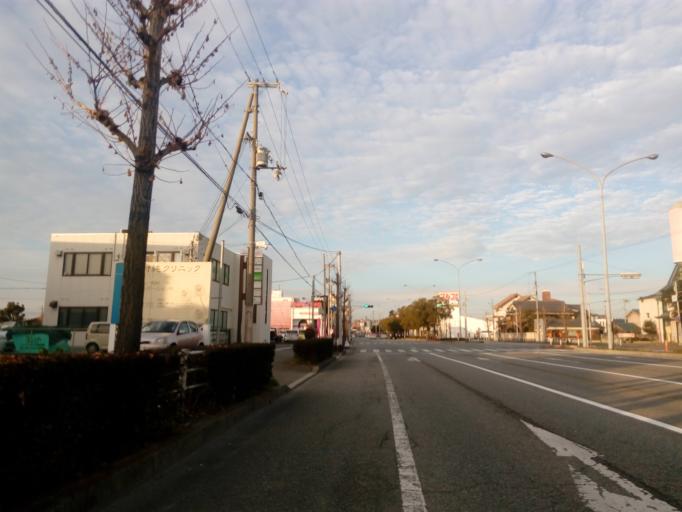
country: JP
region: Hyogo
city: Himeji
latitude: 34.8035
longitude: 134.6799
